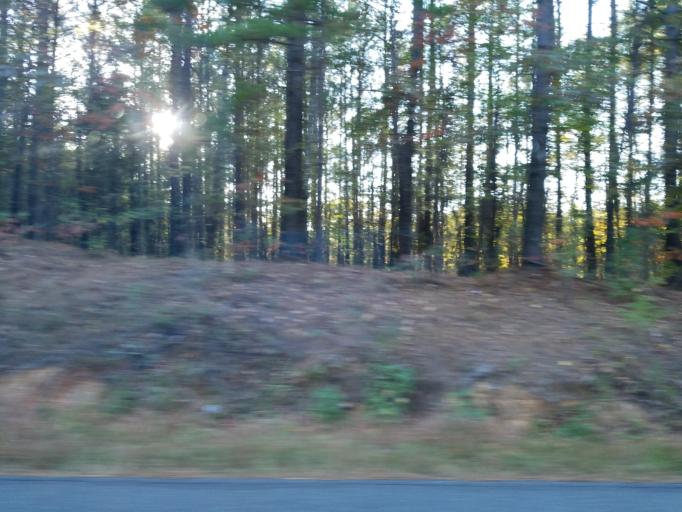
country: US
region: Georgia
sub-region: Bartow County
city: Euharlee
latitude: 34.2176
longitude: -84.9352
